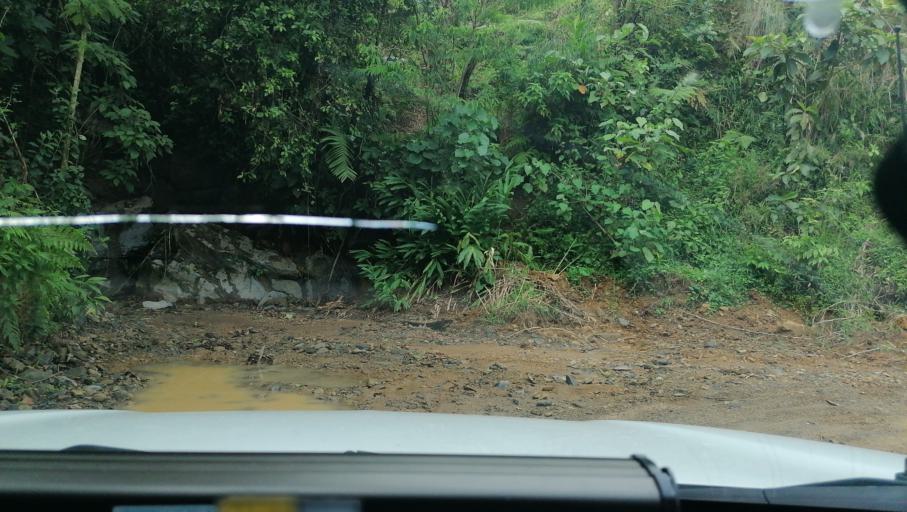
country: MX
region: Chiapas
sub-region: Tapilula
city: San Francisco Jacona
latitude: 17.3068
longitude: -93.1028
